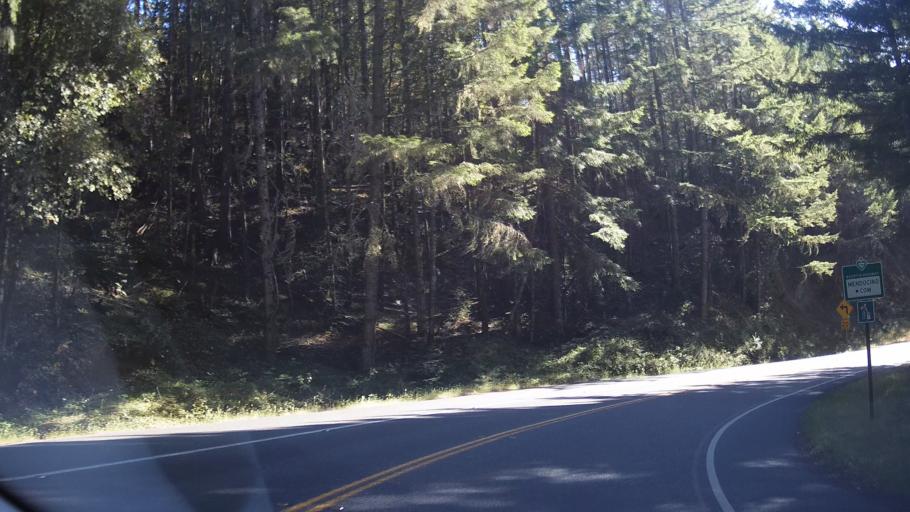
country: US
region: California
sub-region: Mendocino County
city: Brooktrails
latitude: 39.3910
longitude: -123.4663
